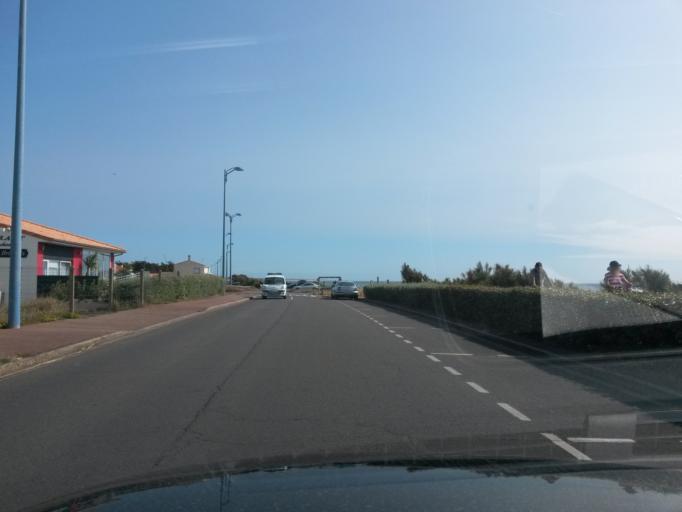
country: FR
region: Pays de la Loire
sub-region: Departement de la Vendee
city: Bretignolles-sur-Mer
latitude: 46.6197
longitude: -1.8720
